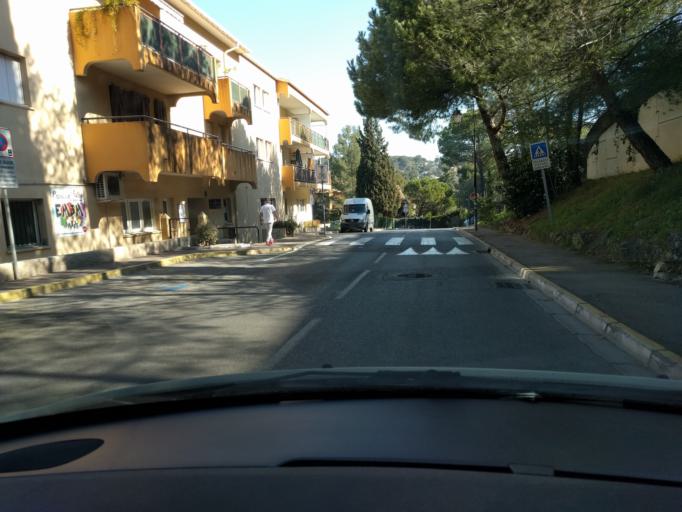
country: FR
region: Provence-Alpes-Cote d'Azur
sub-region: Departement des Alpes-Maritimes
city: Mougins
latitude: 43.6008
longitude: 6.9870
